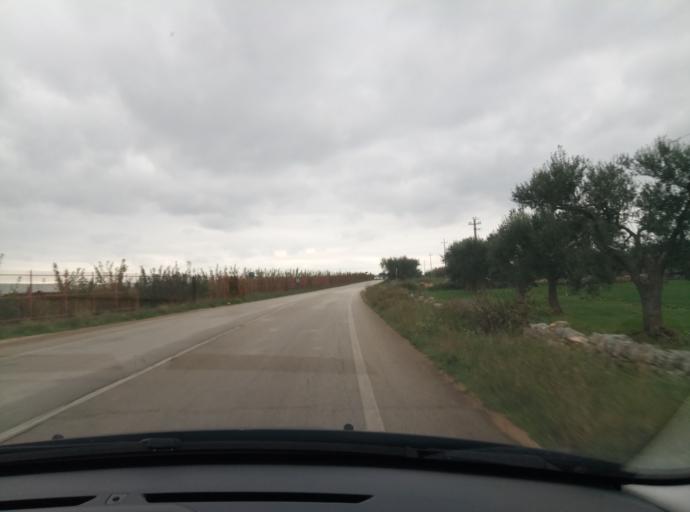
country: IT
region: Apulia
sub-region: Provincia di Bari
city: Acquaviva delle Fonti
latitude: 40.9425
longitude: 16.8666
